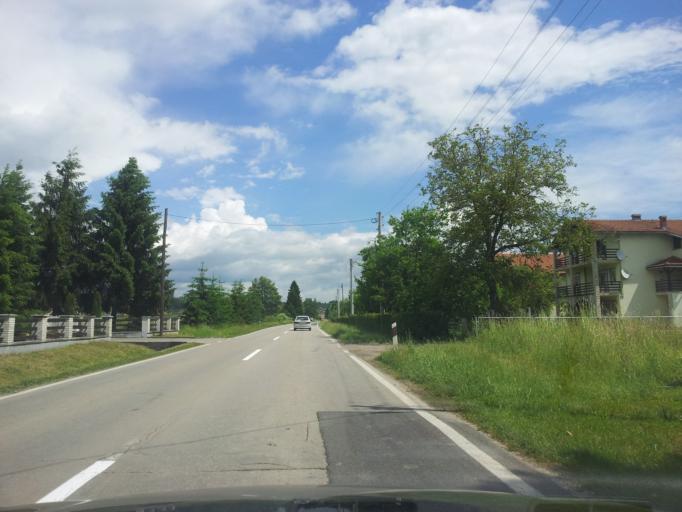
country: HR
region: Karlovacka
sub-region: Grad Karlovac
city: Karlovac
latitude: 45.5553
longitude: 15.5762
